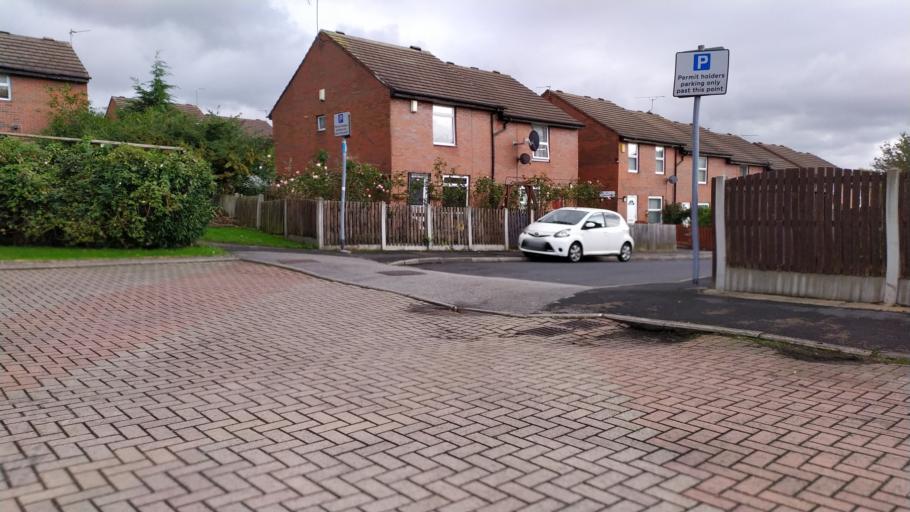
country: GB
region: England
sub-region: City and Borough of Leeds
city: Leeds
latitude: 53.8135
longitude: -1.5510
